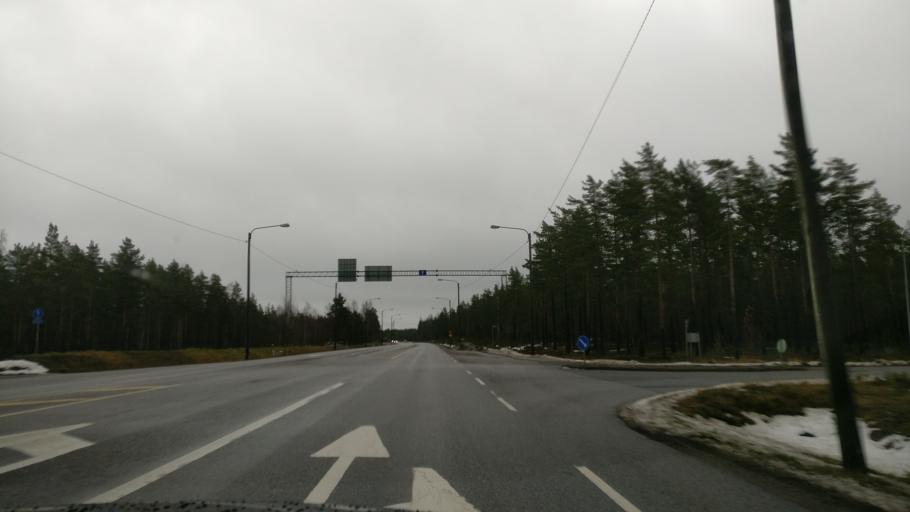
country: FI
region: Uusimaa
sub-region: Raaseporin
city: Hanko
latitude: 59.8565
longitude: 23.0221
